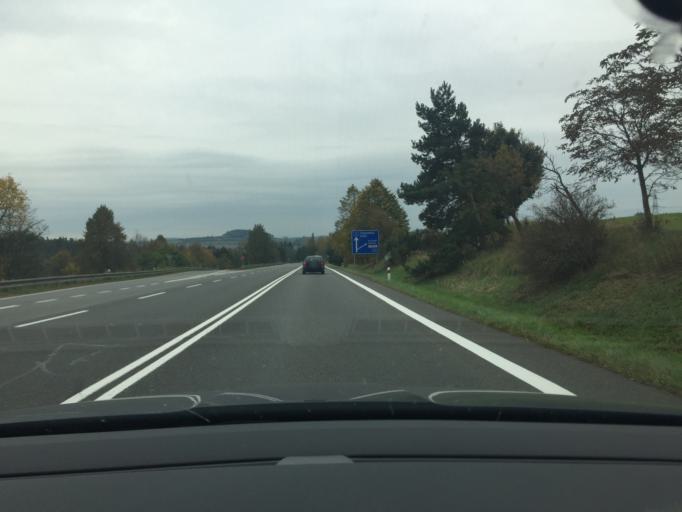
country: CZ
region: Jihocesky
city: Mirotice
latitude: 49.4421
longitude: 14.0551
